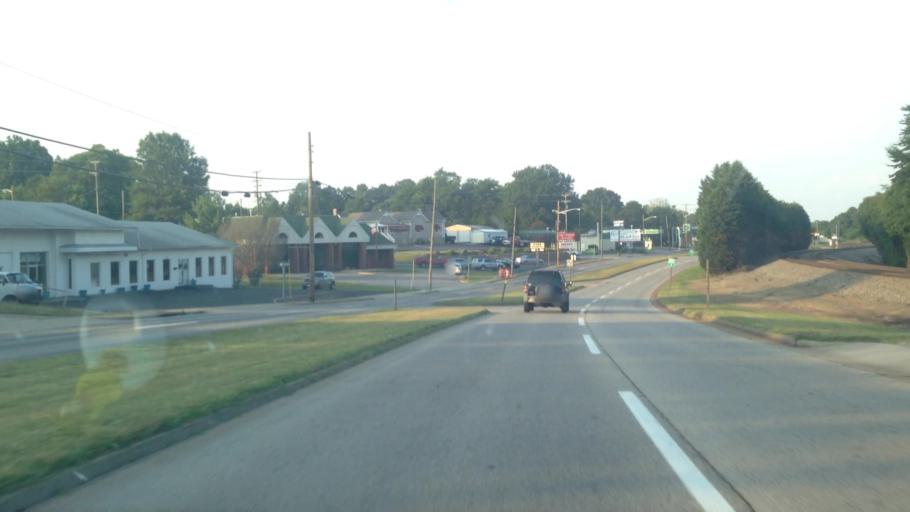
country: US
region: Virginia
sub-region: City of Danville
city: Danville
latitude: 36.5603
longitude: -79.4560
